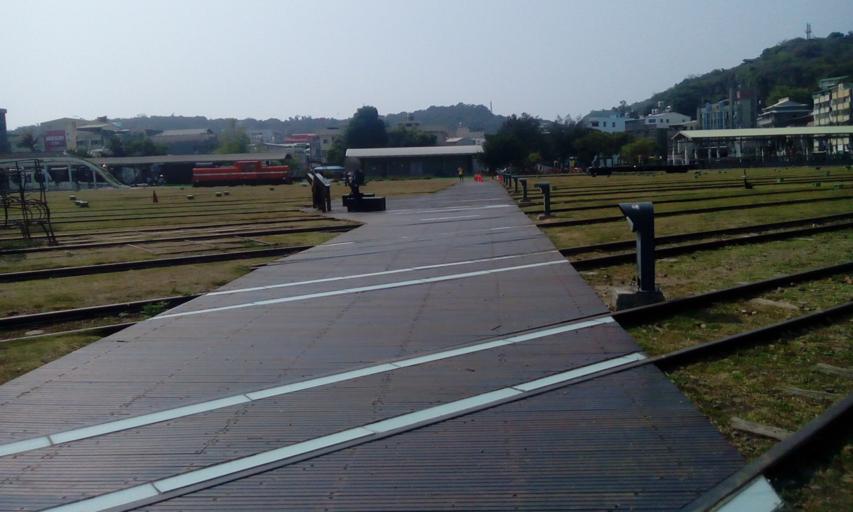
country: TW
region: Kaohsiung
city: Kaohsiung
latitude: 22.6218
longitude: 120.2771
